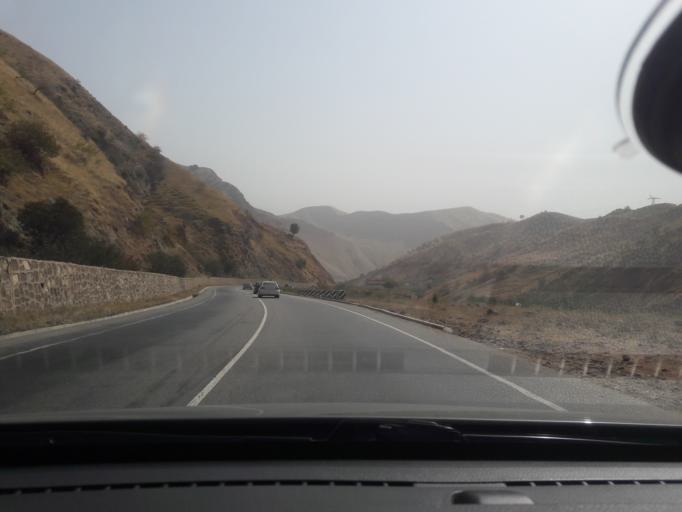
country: TJ
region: Khatlon
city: Norak
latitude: 38.4303
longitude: 69.2244
